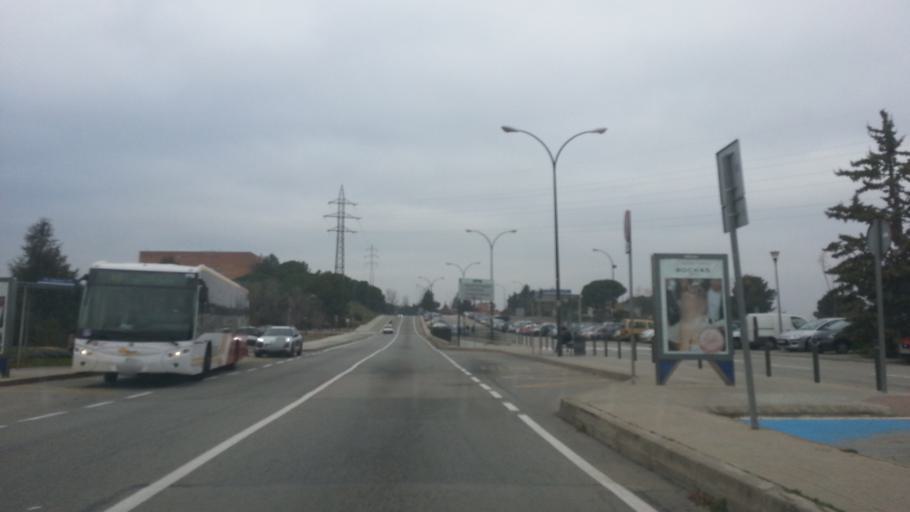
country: ES
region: Catalonia
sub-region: Provincia de Barcelona
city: Barbera del Valles
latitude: 41.5056
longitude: 2.1056
